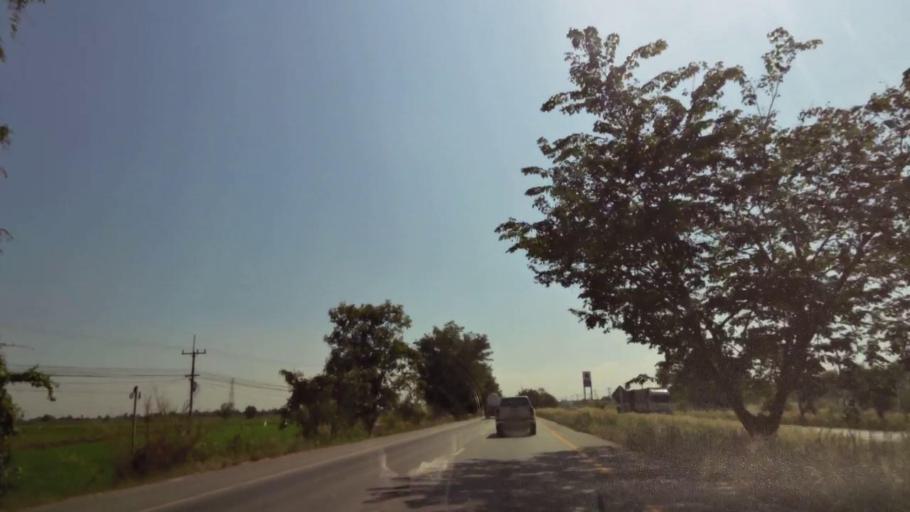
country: TH
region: Nakhon Sawan
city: Kao Liao
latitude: 15.8355
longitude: 100.1177
